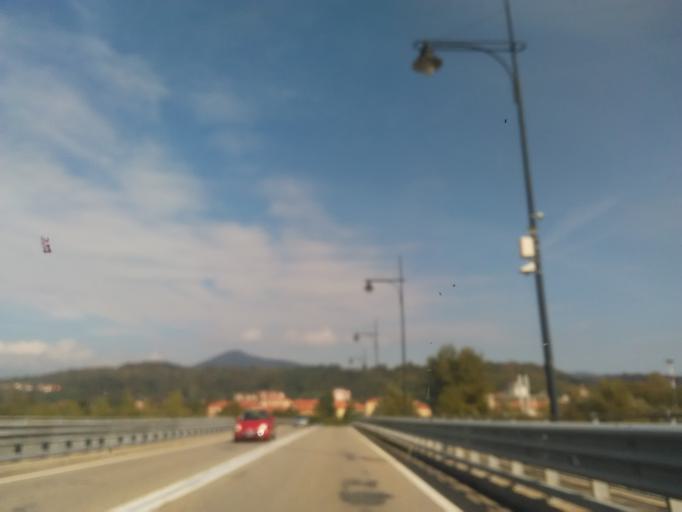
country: IT
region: Piedmont
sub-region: Provincia di Vercelli
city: Borgosesia
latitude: 45.7133
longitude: 8.2671
